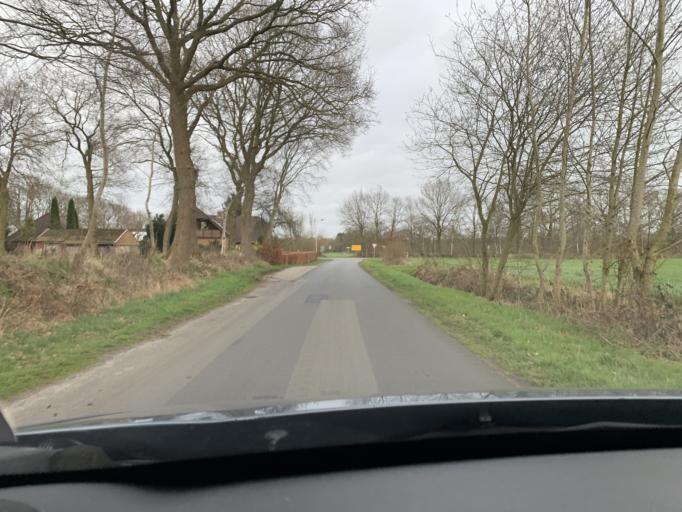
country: DE
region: Lower Saxony
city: Schwerinsdorf
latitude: 53.2668
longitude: 7.7068
